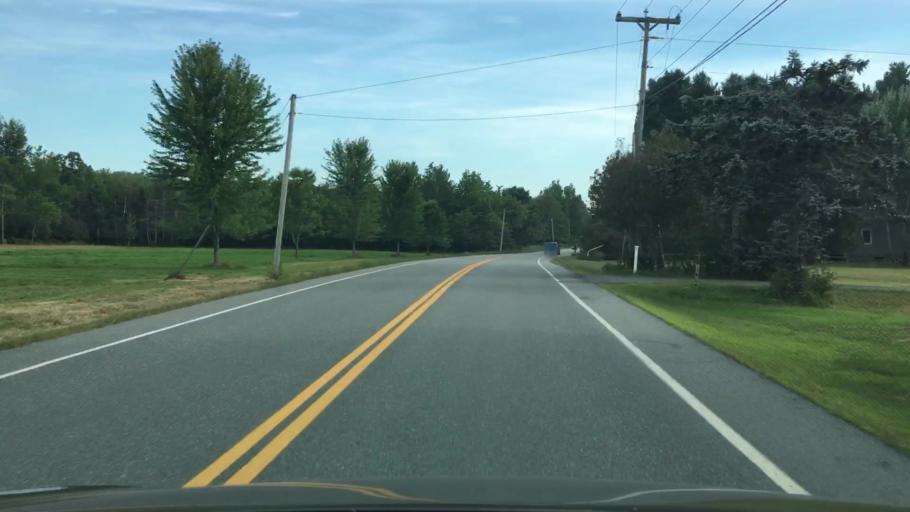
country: US
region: Maine
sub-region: Hancock County
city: Penobscot
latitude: 44.4581
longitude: -68.7804
